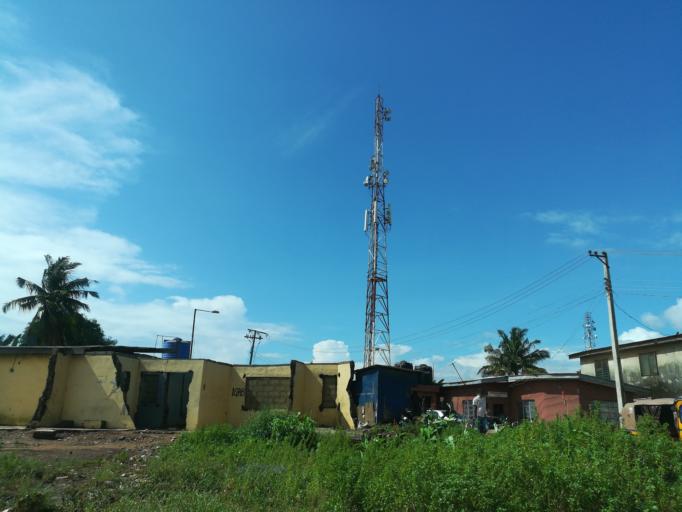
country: NG
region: Lagos
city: Ikorodu
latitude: 6.5923
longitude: 3.5192
